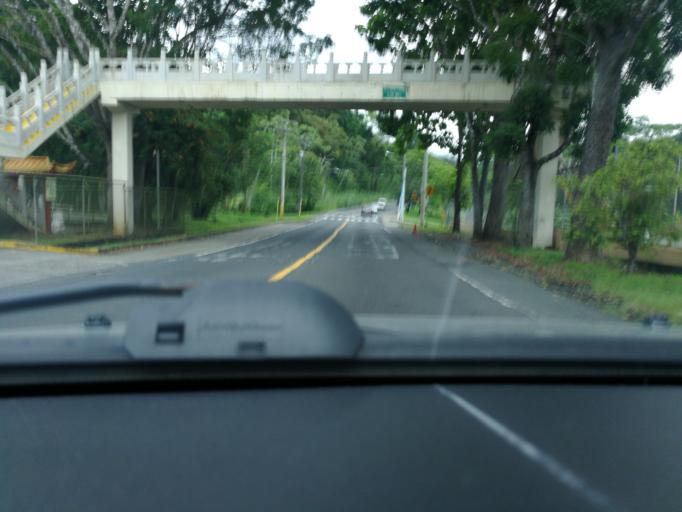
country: PA
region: Panama
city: Panama
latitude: 9.0044
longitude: -79.5456
